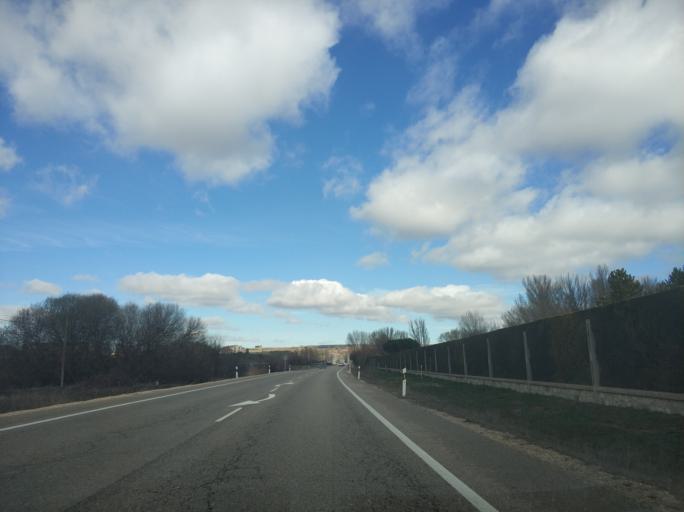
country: ES
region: Castille and Leon
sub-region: Provincia de Burgos
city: Sarracin
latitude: 42.2558
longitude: -3.6915
